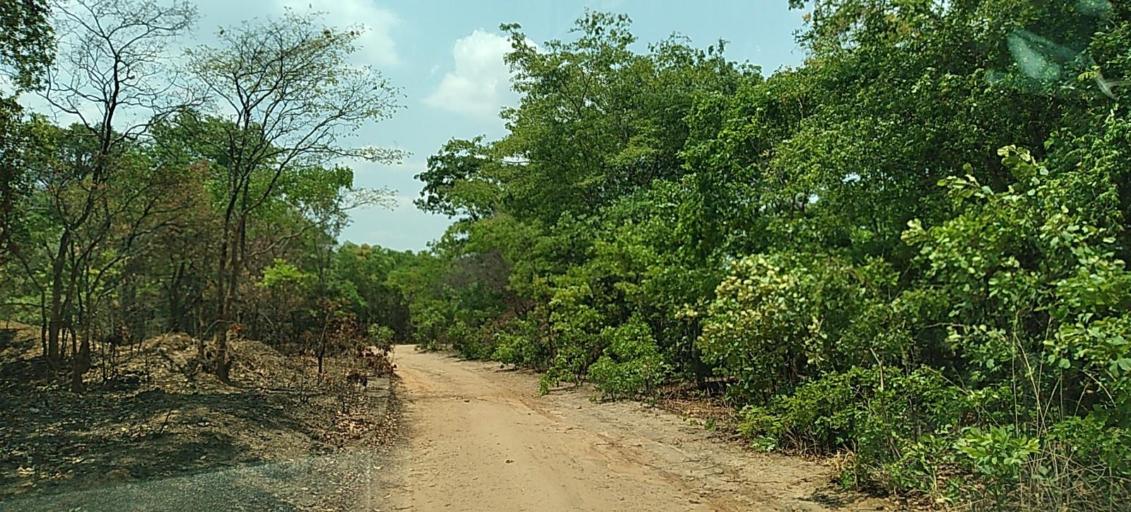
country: ZM
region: Copperbelt
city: Luanshya
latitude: -13.0913
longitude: 28.2870
